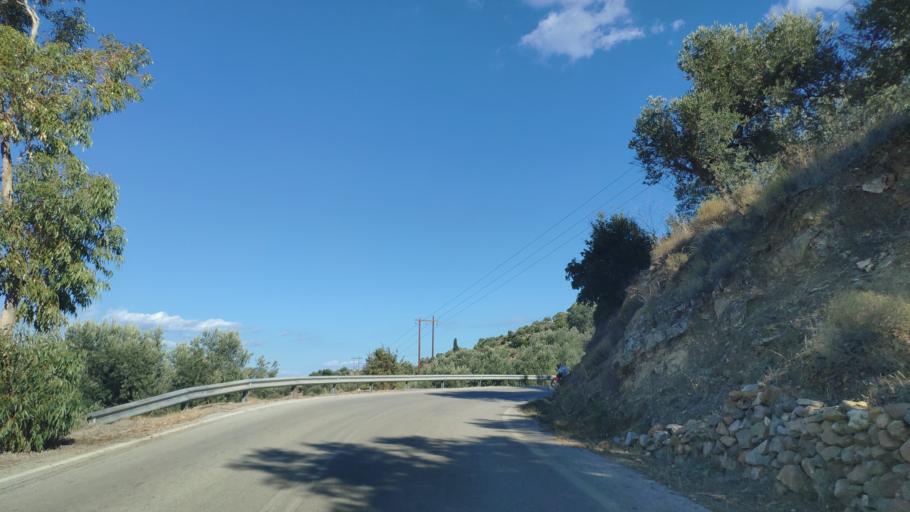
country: GR
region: Attica
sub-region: Nomos Piraios
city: Galatas
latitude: 37.5386
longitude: 23.3578
